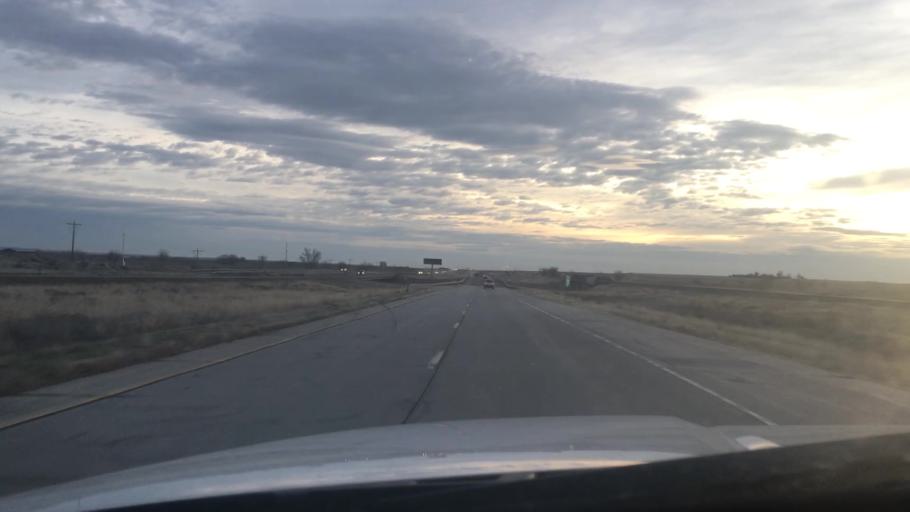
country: US
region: Colorado
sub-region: Morgan County
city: Fort Morgan
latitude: 40.2476
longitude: -104.0397
